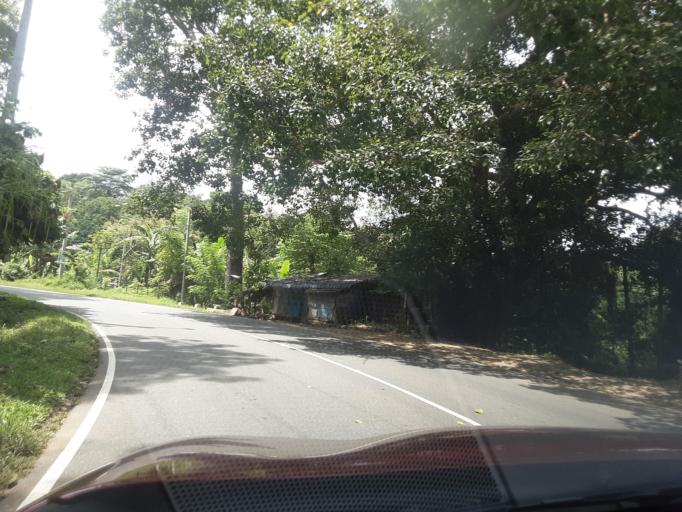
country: LK
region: Uva
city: Monaragala
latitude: 6.8963
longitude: 81.2480
